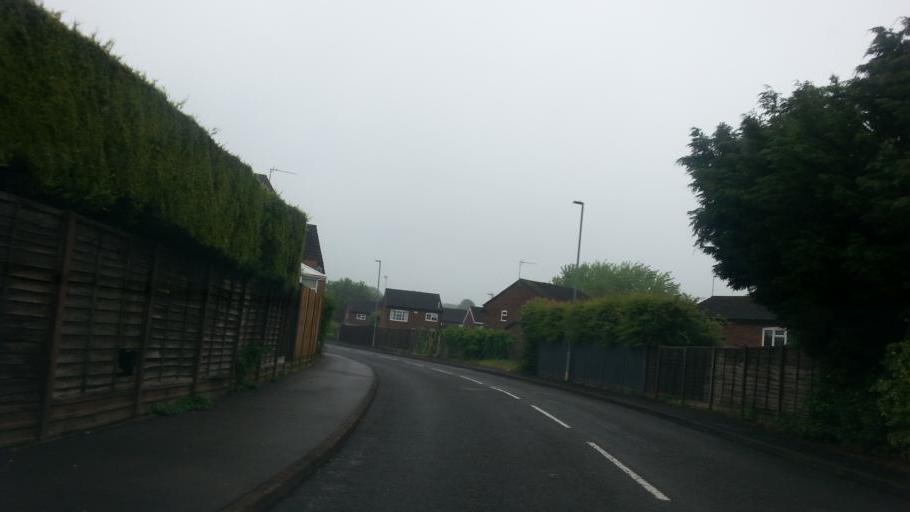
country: GB
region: England
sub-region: Leicestershire
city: Oadby
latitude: 52.5947
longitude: -1.0625
